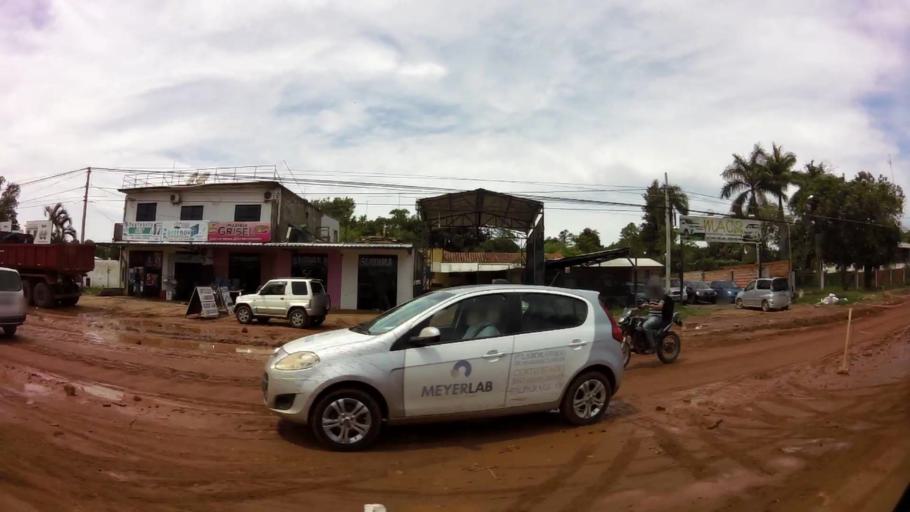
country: PY
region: Central
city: Limpio
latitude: -25.1955
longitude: -57.5113
